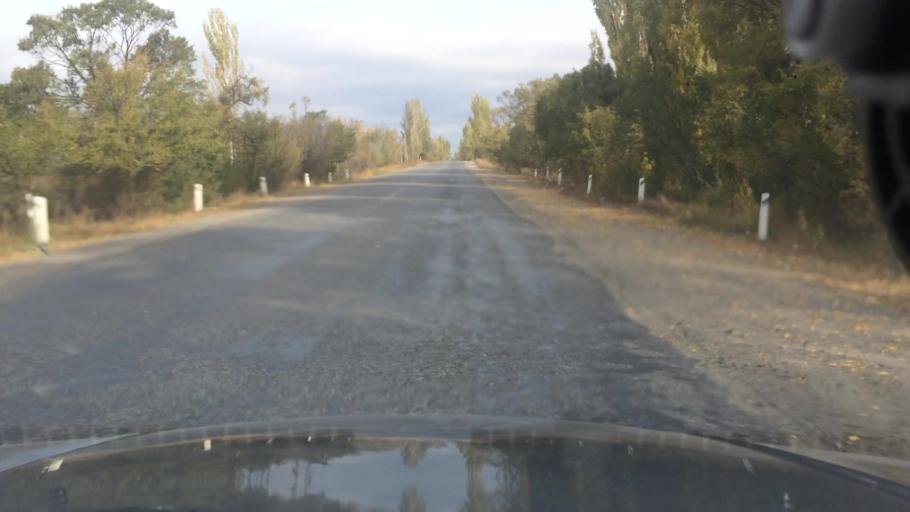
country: KG
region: Ysyk-Koel
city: Karakol
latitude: 42.5673
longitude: 78.3911
